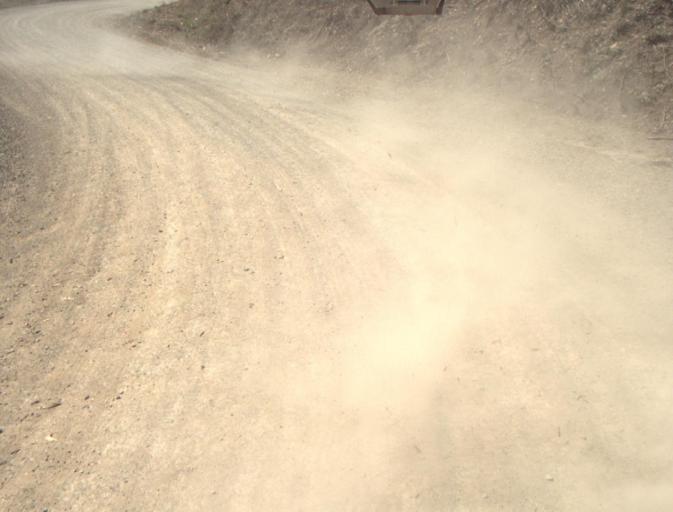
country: AU
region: Tasmania
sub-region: Dorset
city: Scottsdale
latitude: -41.3227
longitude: 147.4150
